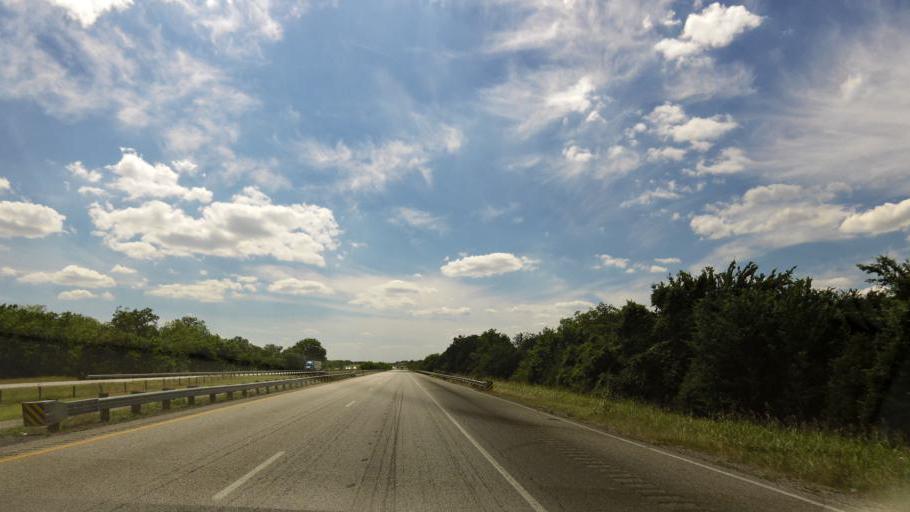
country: US
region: Texas
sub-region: Gonzales County
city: Waelder
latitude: 29.6631
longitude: -97.3784
